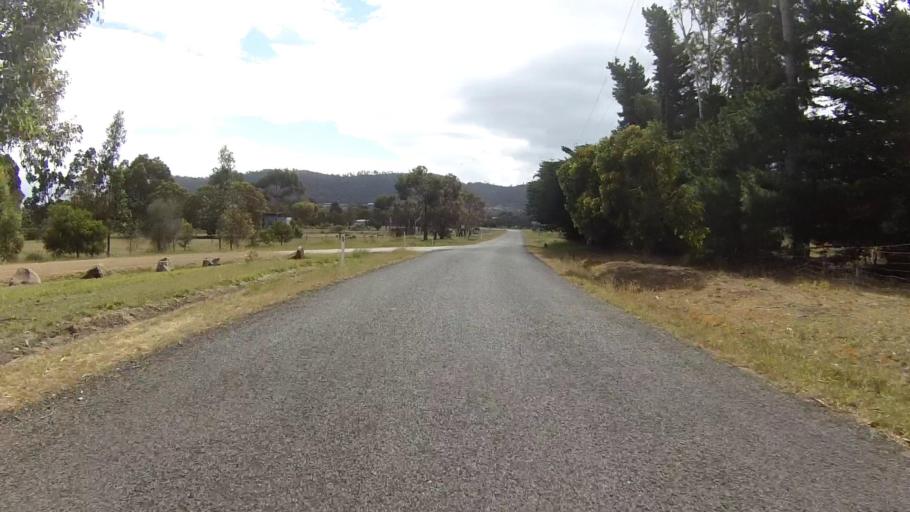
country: AU
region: Tasmania
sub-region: Clarence
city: Acton Park
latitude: -42.8886
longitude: 147.4997
